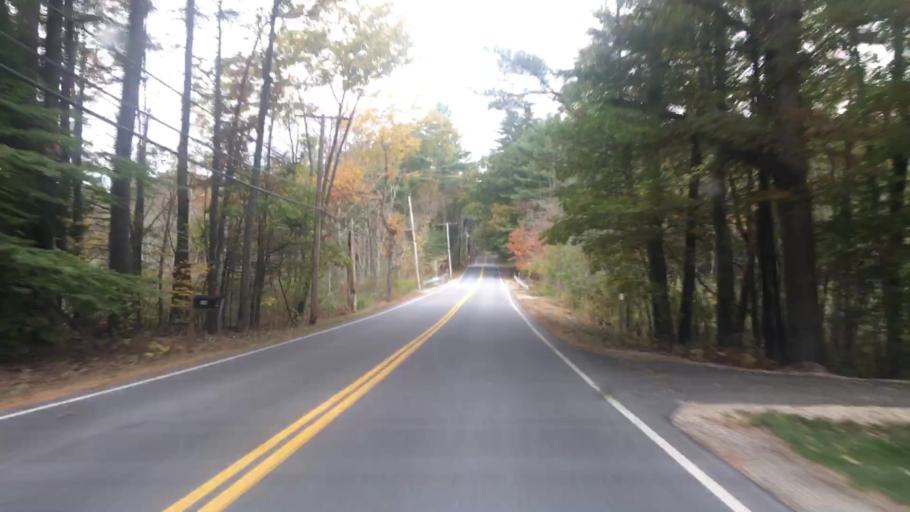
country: US
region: New Hampshire
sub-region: Rockingham County
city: Exeter
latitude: 42.9885
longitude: -70.9992
